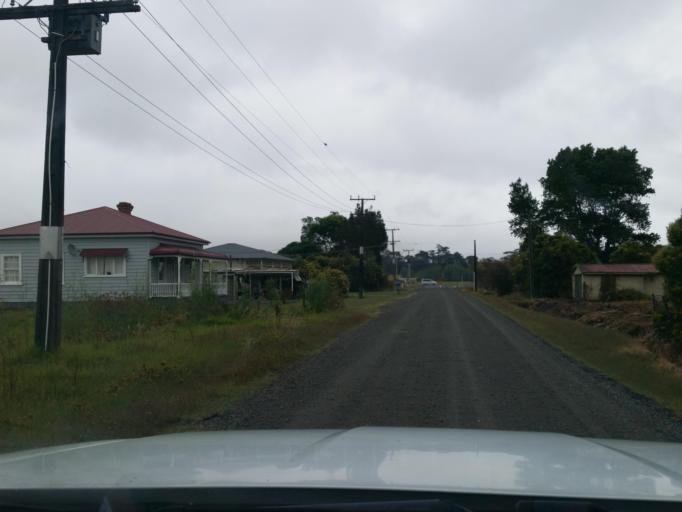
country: NZ
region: Northland
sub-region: Kaipara District
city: Dargaville
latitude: -36.0136
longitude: 173.9046
